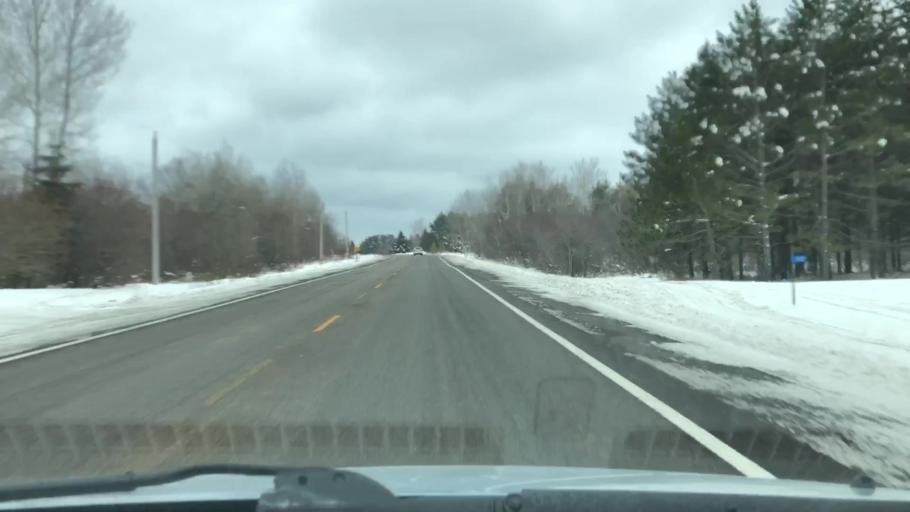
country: US
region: Minnesota
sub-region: Carlton County
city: Esko
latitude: 46.6824
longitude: -92.3683
